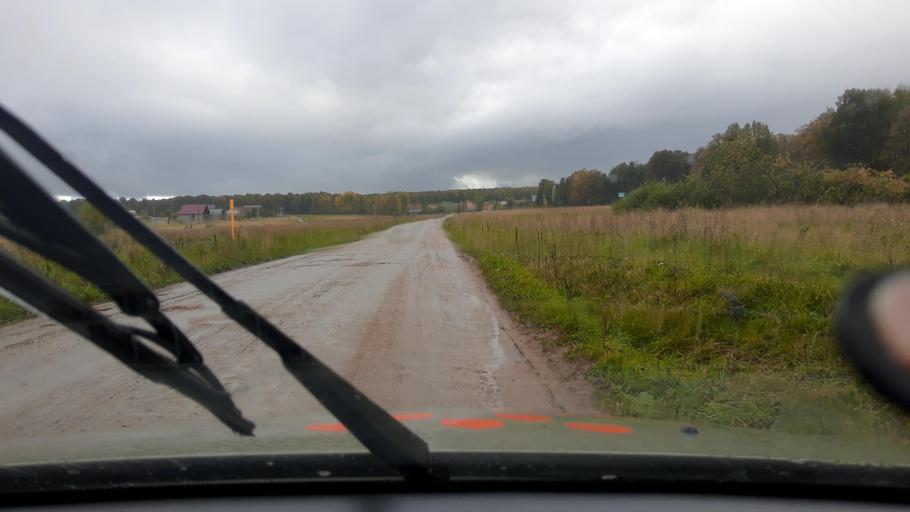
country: RU
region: Bashkortostan
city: Kudeyevskiy
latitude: 54.8793
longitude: 56.6313
